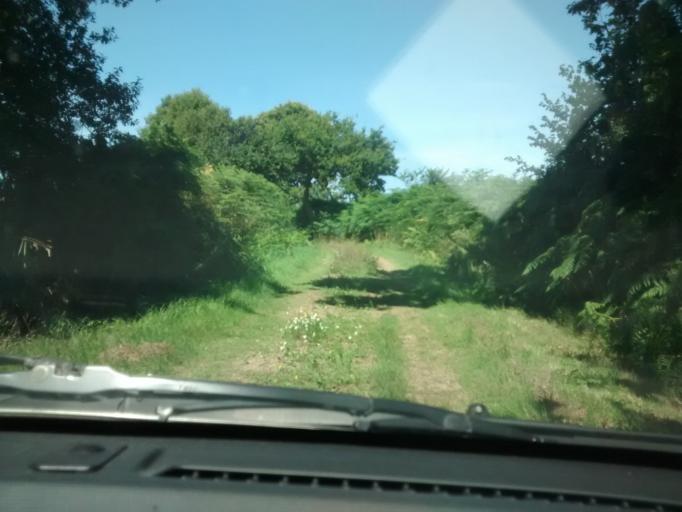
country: FR
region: Brittany
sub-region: Departement des Cotes-d'Armor
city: Trevou-Treguignec
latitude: 48.7763
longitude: -3.3365
